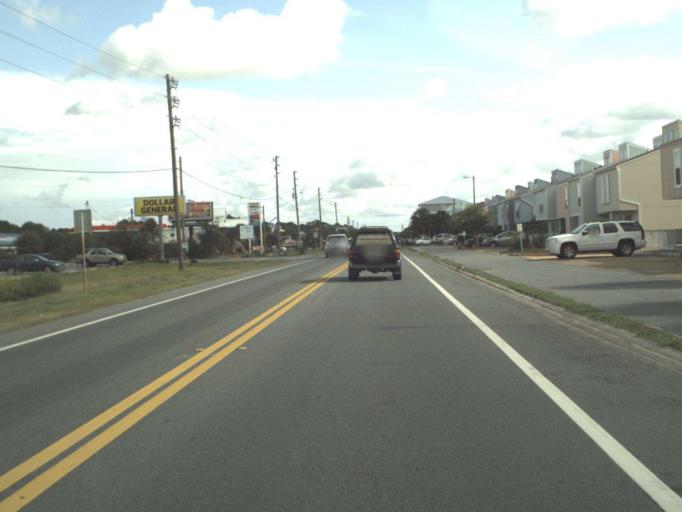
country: US
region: Florida
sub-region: Bay County
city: Mexico Beach
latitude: 29.9114
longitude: -85.3745
